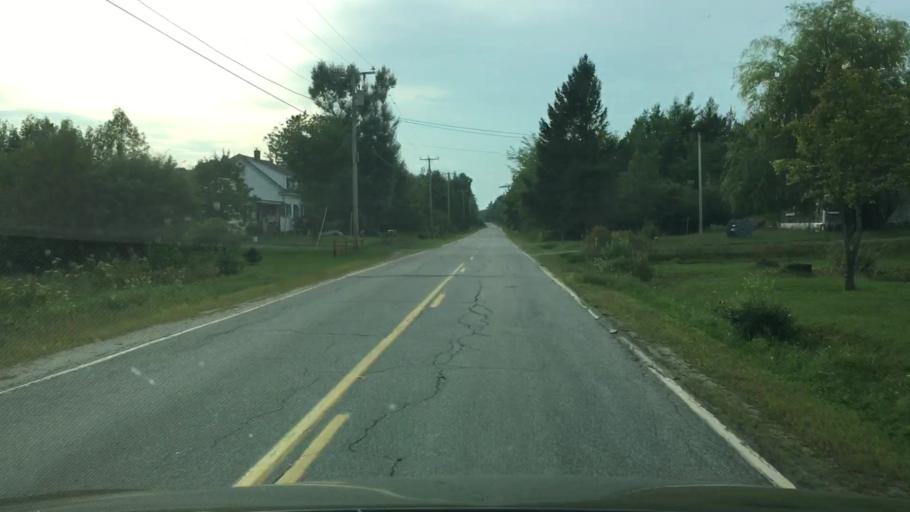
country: US
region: Maine
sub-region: Hancock County
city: Penobscot
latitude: 44.4707
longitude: -68.7462
